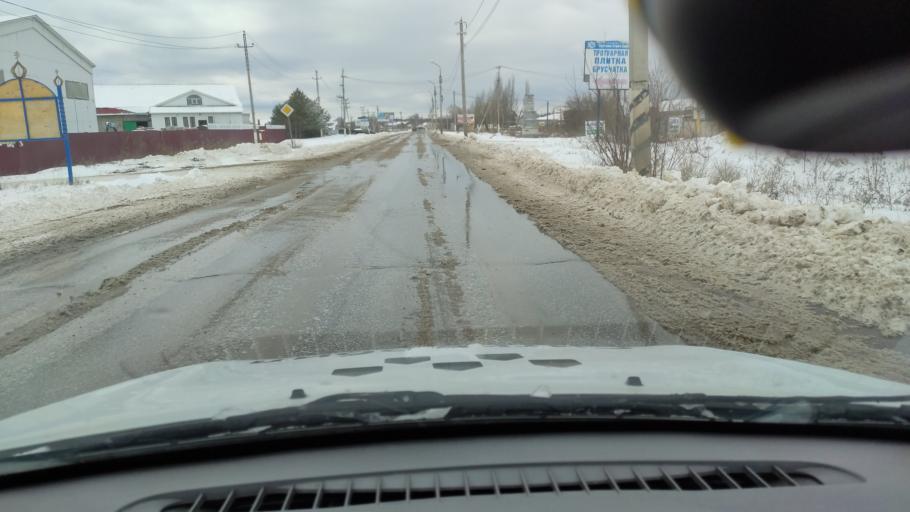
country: RU
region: Samara
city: Tol'yatti
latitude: 53.5726
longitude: 49.4004
